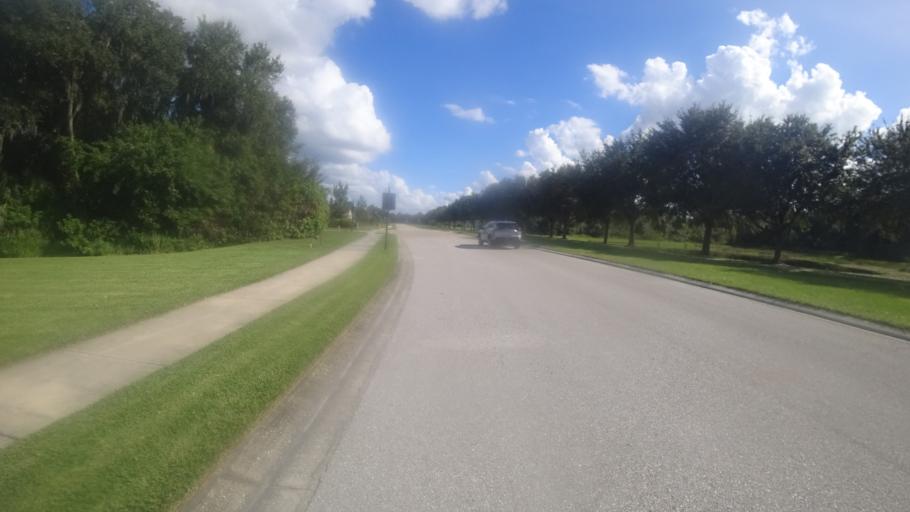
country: US
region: Florida
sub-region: Manatee County
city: Ellenton
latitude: 27.5346
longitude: -82.3840
